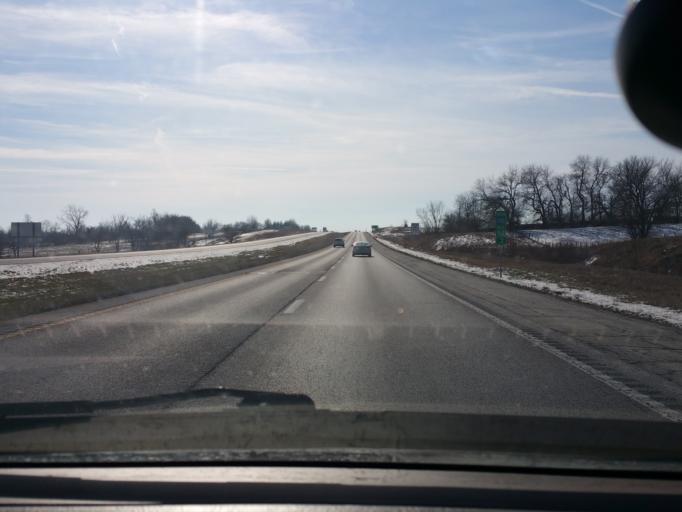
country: US
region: Missouri
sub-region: Clinton County
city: Cameron
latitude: 39.7248
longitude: -94.2215
